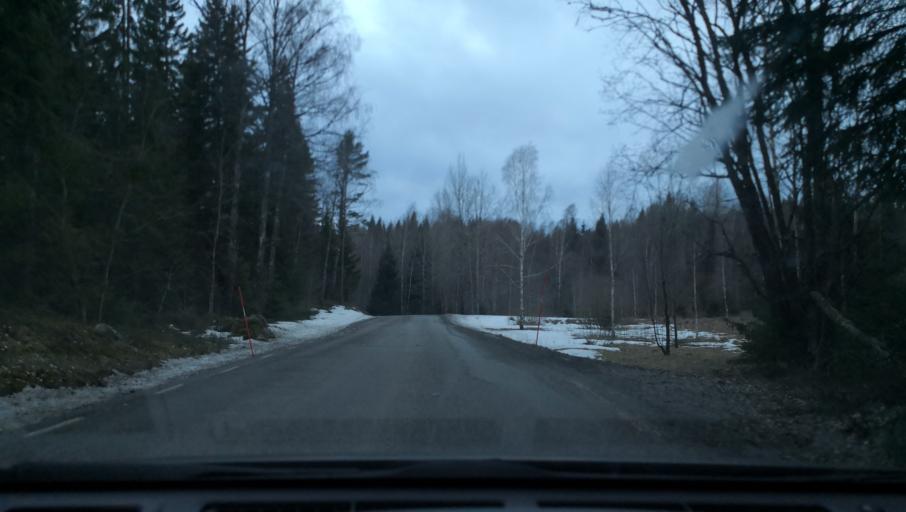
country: SE
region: Vaestmanland
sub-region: Kopings Kommun
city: Kolsva
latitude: 59.5682
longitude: 15.7769
